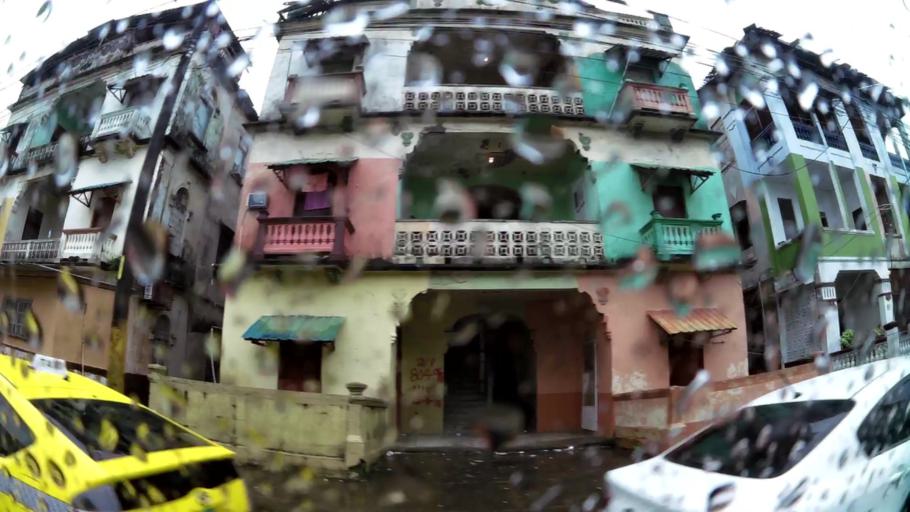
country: PA
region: Colon
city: Colon
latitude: 9.3585
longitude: -79.8990
